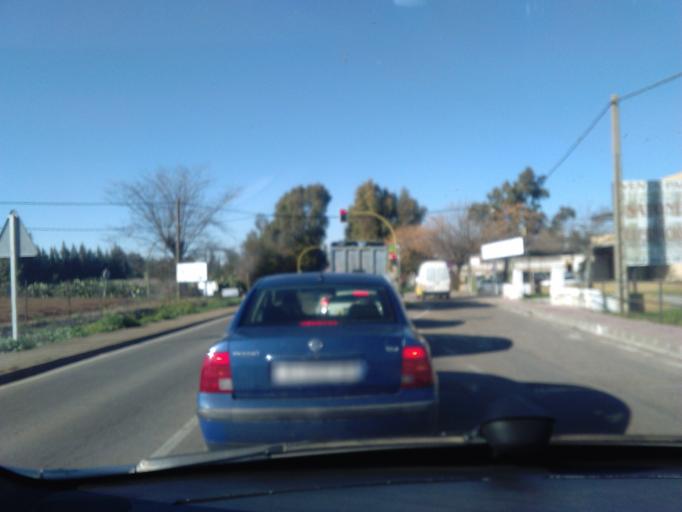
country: ES
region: Andalusia
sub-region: Provincia de Sevilla
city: Sevilla
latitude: 37.4287
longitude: -5.9310
